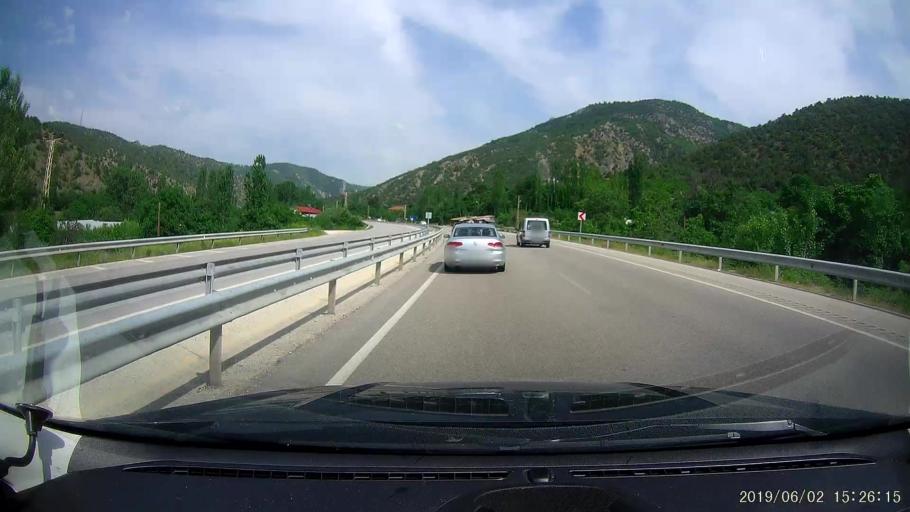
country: TR
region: Amasya
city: Saraycik
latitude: 40.9869
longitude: 35.0329
